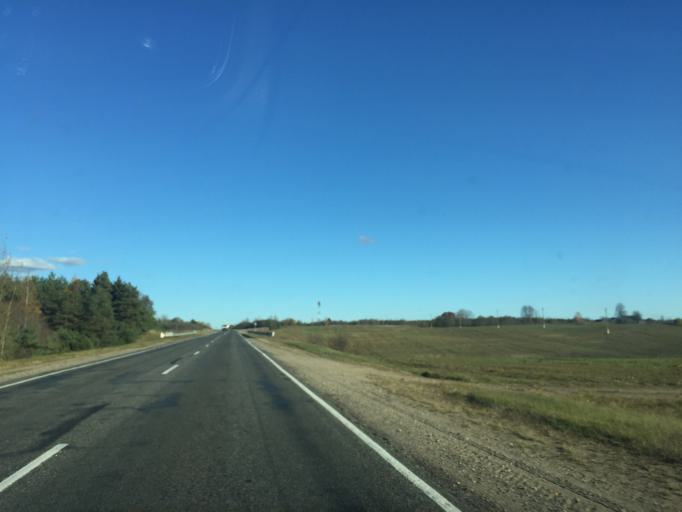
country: BY
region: Vitebsk
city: Dzisna
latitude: 55.2392
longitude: 28.0519
